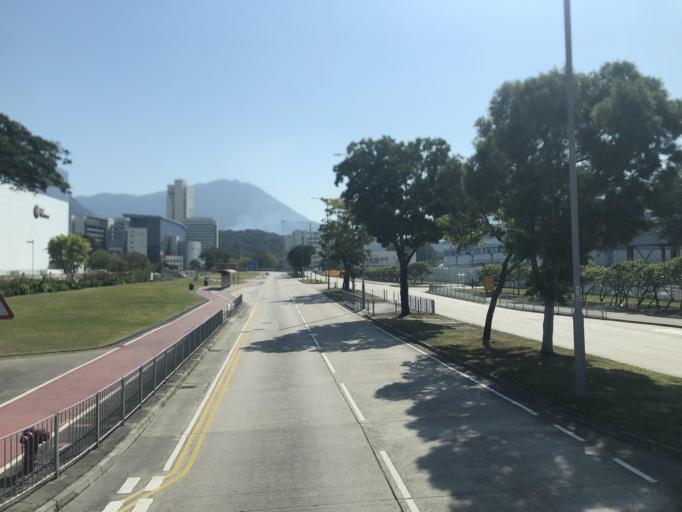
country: HK
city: Tai O
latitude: 22.3020
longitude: 113.9310
